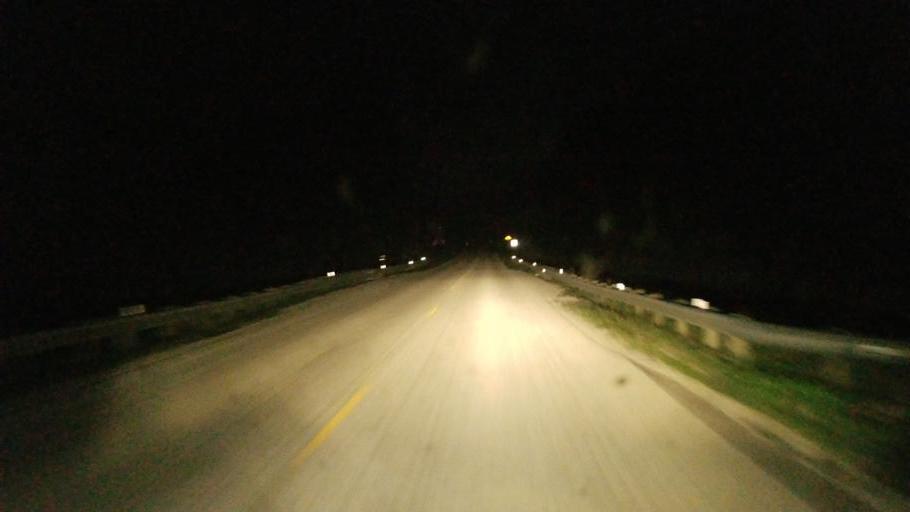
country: US
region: Ohio
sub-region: Sandusky County
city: Bellville
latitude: 40.5973
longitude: -82.5832
